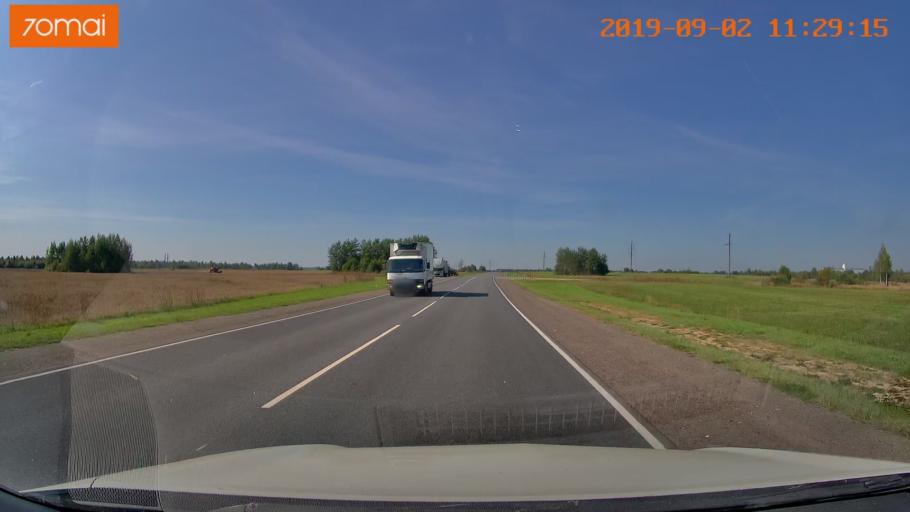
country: RU
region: Smolensk
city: Roslavl'
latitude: 53.9903
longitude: 32.8687
